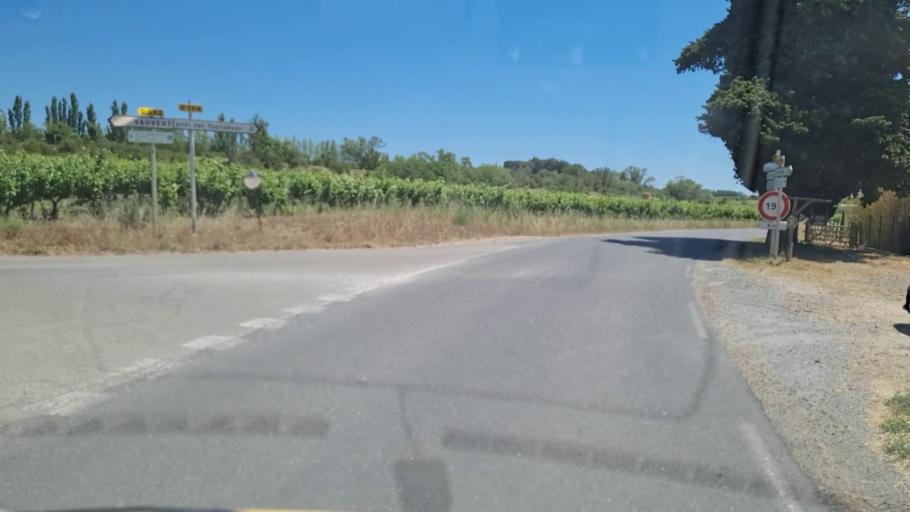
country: FR
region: Languedoc-Roussillon
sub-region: Departement du Gard
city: Le Cailar
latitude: 43.6680
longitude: 4.2598
